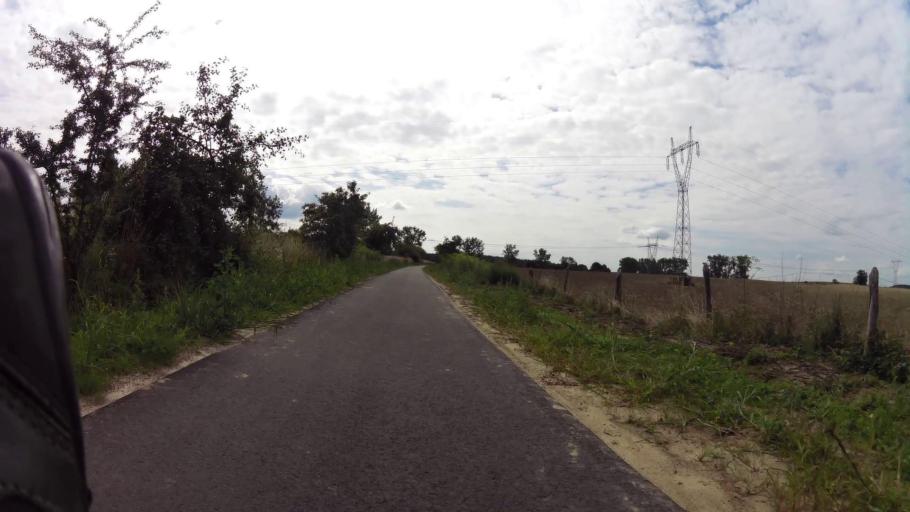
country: PL
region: West Pomeranian Voivodeship
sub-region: Powiat pyrzycki
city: Bielice
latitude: 53.2160
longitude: 14.6087
